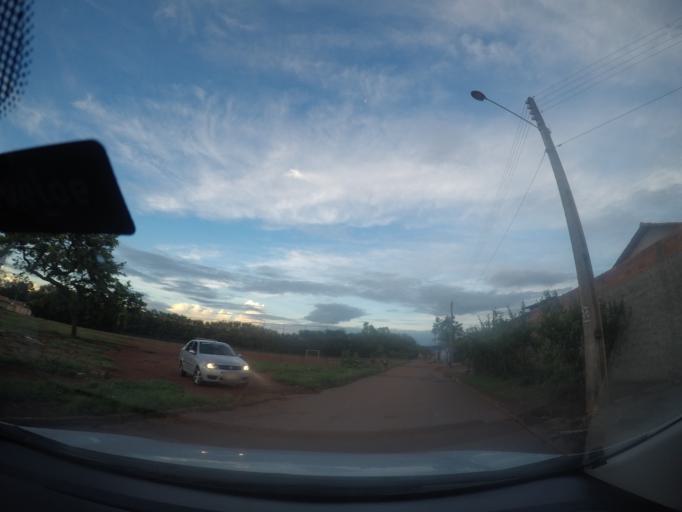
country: BR
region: Goias
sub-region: Goianira
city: Goianira
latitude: -16.5709
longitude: -49.3823
